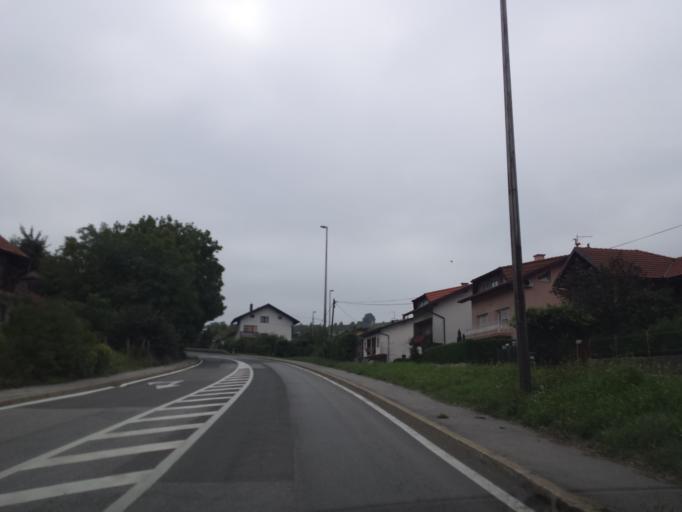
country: HR
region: Karlovacka
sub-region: Grad Karlovac
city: Karlovac
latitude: 45.4523
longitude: 15.4919
